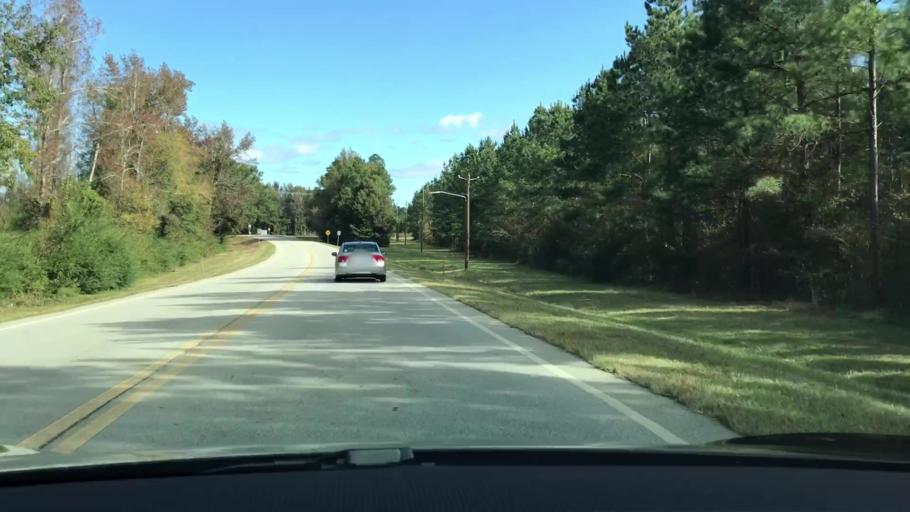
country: US
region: Georgia
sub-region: Jefferson County
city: Wrens
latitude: 33.2215
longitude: -82.4638
